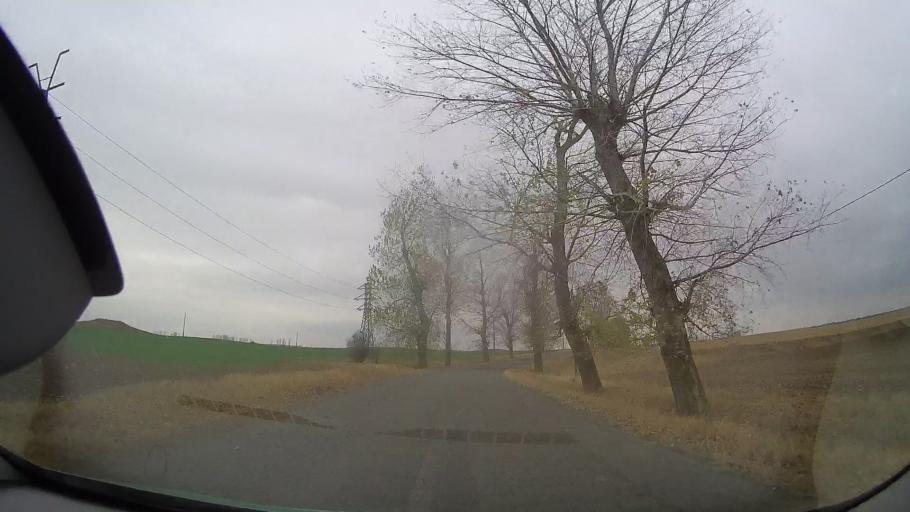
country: RO
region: Buzau
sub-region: Comuna Rusetu
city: Rusetu
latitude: 44.9418
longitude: 27.2455
